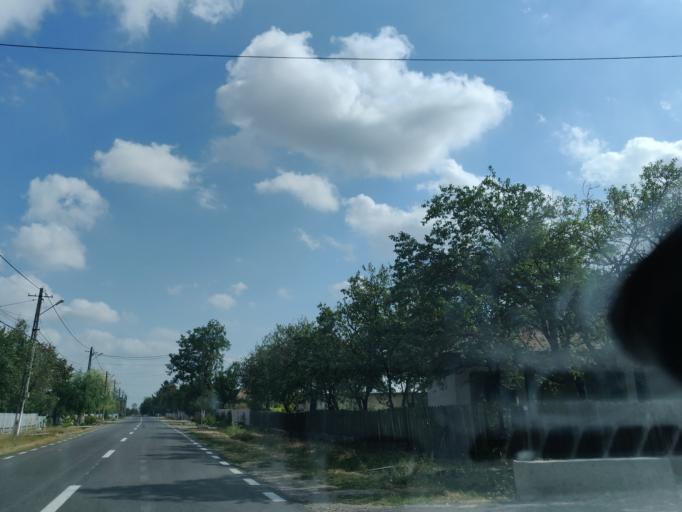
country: RO
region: Vrancea
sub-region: Comuna Ciorasti
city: Mihalceni
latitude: 45.4359
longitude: 27.3177
